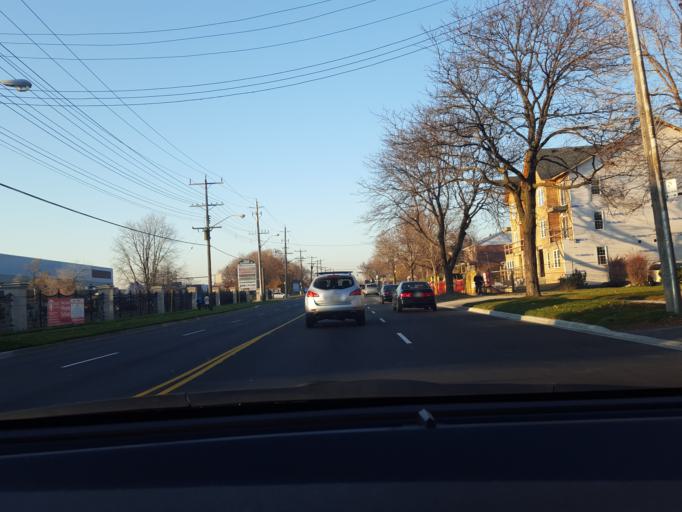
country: CA
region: Ontario
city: Scarborough
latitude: 43.7565
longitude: -79.2885
